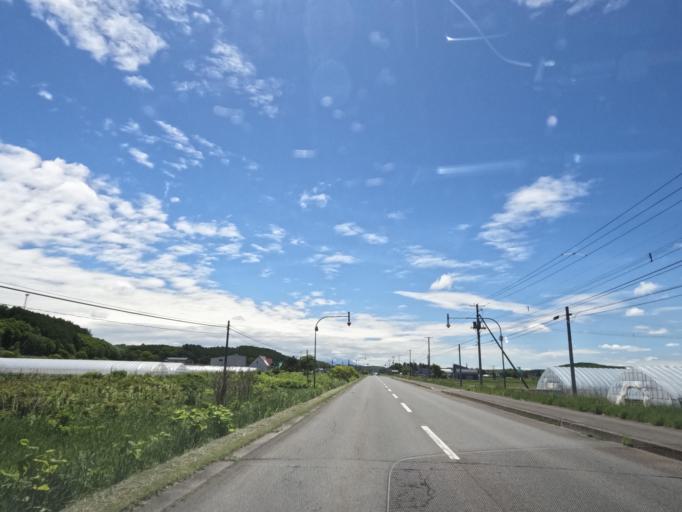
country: JP
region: Hokkaido
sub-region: Asahikawa-shi
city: Asahikawa
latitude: 43.6957
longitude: 142.3856
